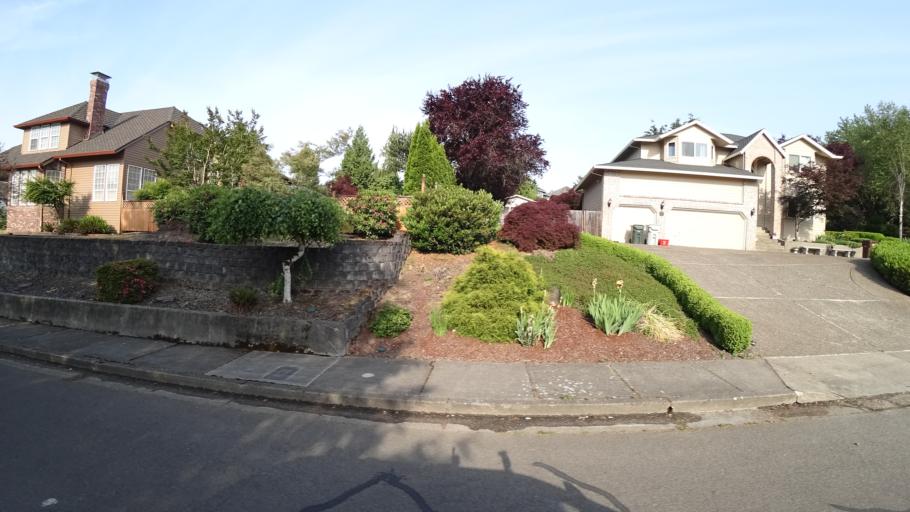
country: US
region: Oregon
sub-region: Clackamas County
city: Happy Valley
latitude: 45.4490
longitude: -122.5294
